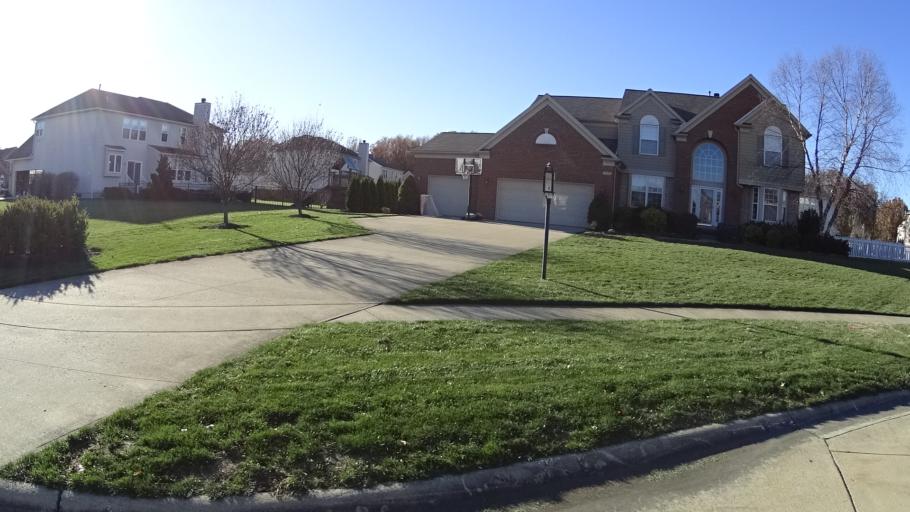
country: US
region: Ohio
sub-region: Lorain County
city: Avon Center
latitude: 41.4486
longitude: -82.0096
